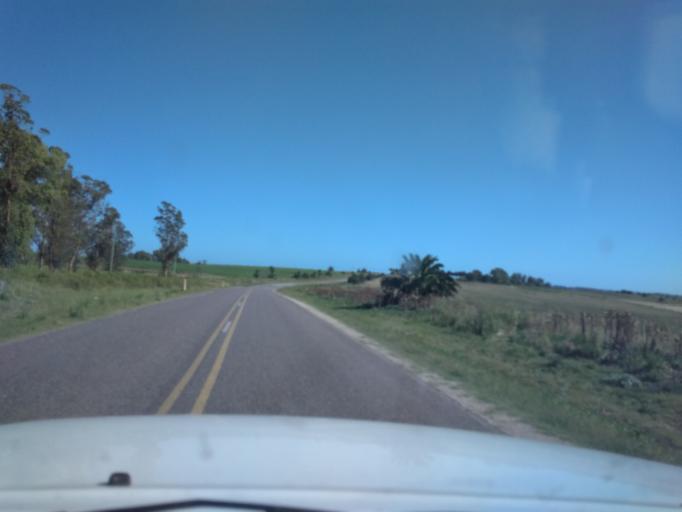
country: UY
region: Canelones
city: San Ramon
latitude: -34.1643
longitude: -55.9466
